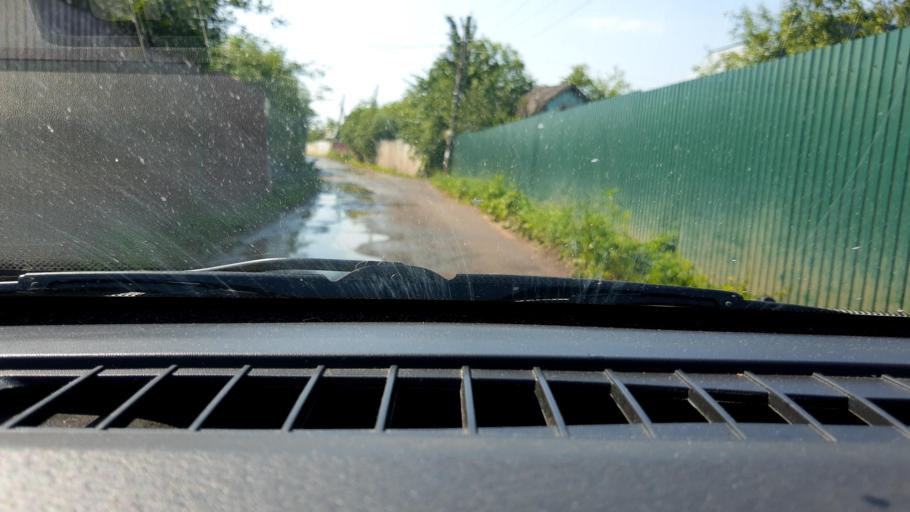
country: RU
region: Nizjnij Novgorod
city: Gorbatovka
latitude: 56.3192
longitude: 43.8287
